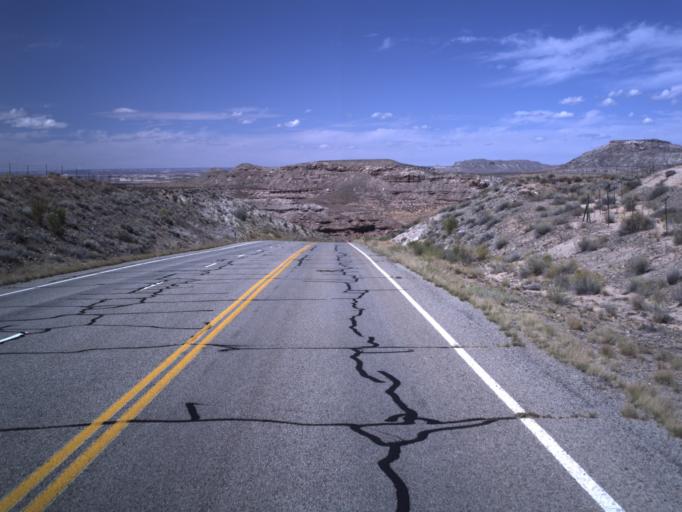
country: US
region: Utah
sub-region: San Juan County
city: Blanding
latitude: 37.2806
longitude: -109.3761
